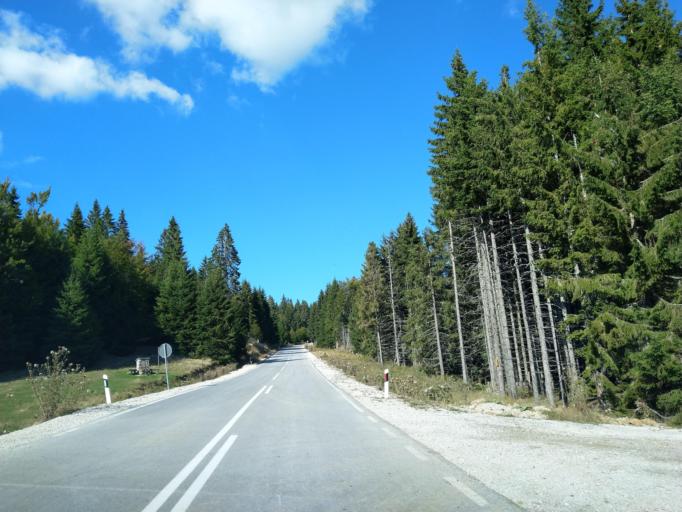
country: RS
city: Sokolovica
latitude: 43.2982
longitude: 20.3063
